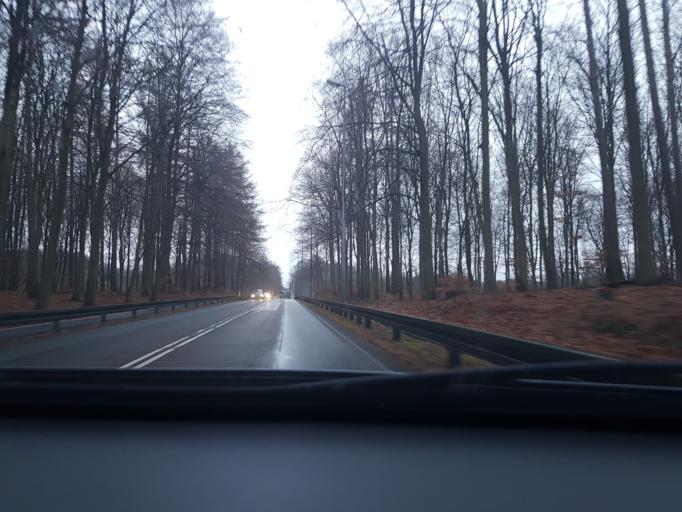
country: DK
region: Capital Region
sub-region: Fureso Kommune
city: Vaerlose
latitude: 55.7614
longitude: 12.3681
